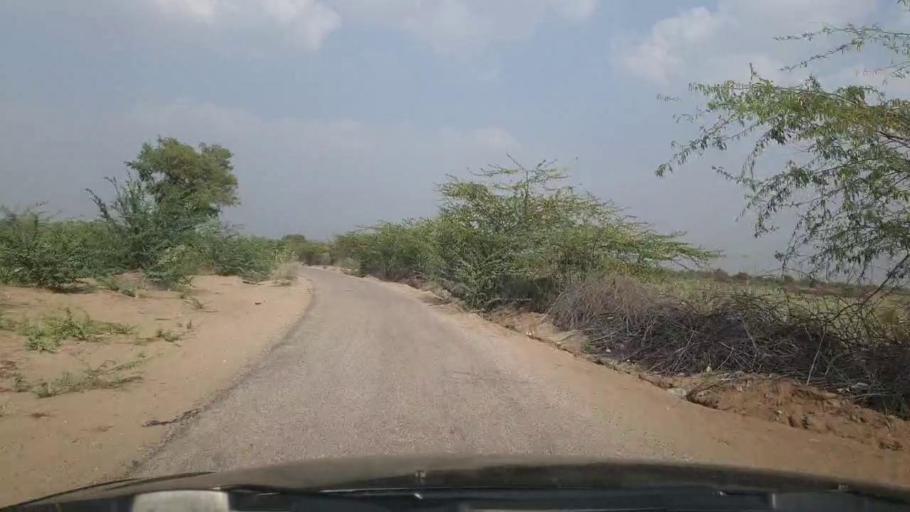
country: PK
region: Sindh
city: Islamkot
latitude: 25.0236
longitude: 70.5550
